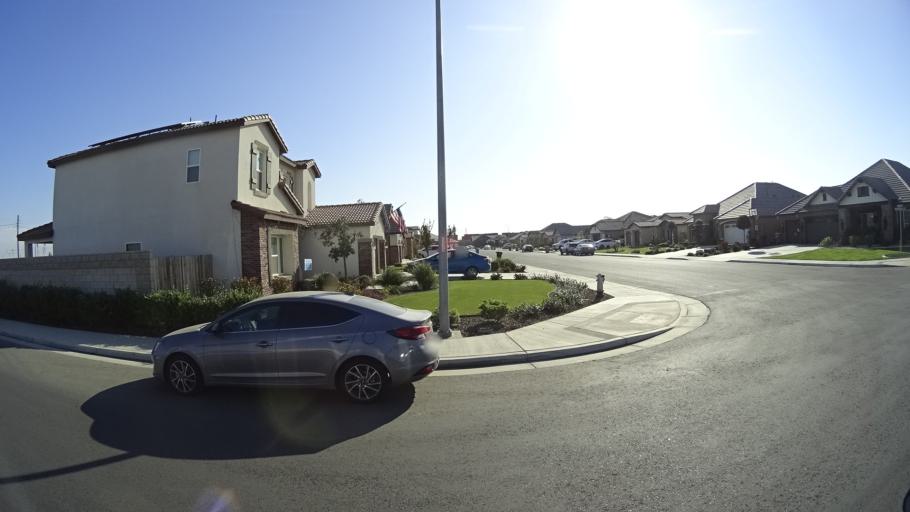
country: US
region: California
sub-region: Kern County
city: Greenacres
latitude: 35.3785
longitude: -119.1015
